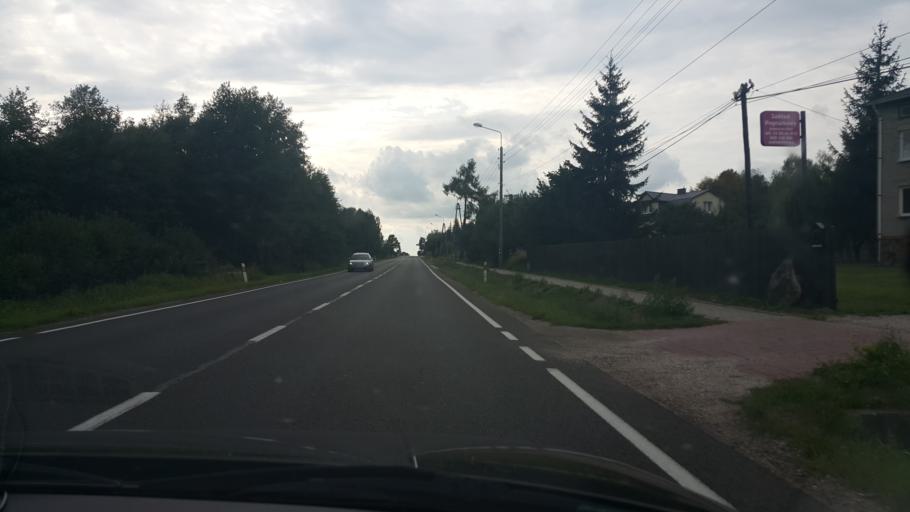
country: PL
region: Swietokrzyskie
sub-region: Powiat skarzyski
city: Blizyn
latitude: 51.1015
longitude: 20.7864
